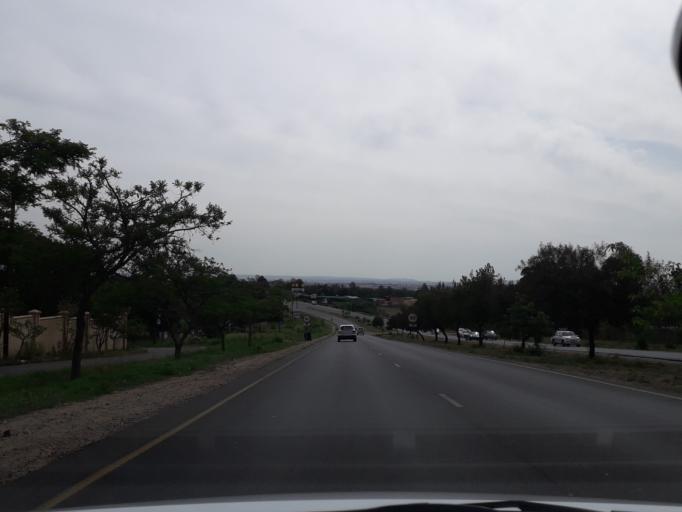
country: ZA
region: Gauteng
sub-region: City of Johannesburg Metropolitan Municipality
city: Diepsloot
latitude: -25.9866
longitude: 28.0577
